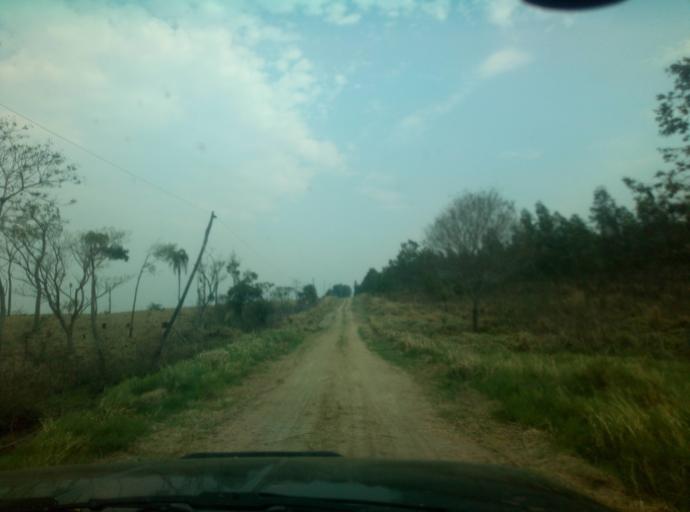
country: PY
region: Caaguazu
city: San Joaquin
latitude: -25.1086
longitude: -56.1275
